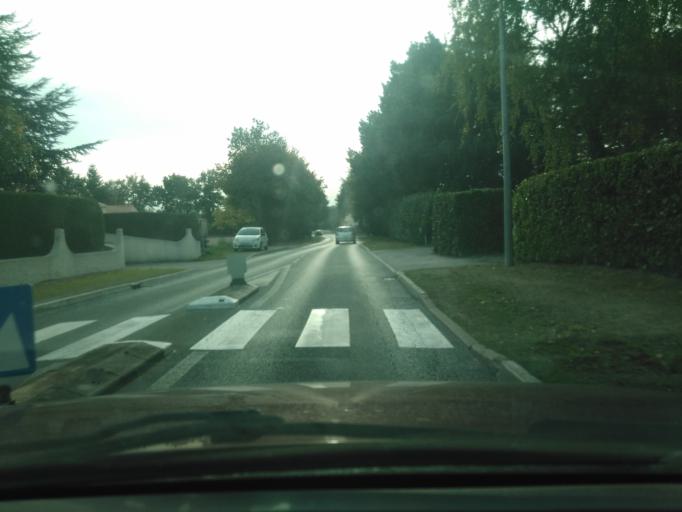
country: FR
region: Pays de la Loire
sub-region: Departement de la Vendee
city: Dompierre-sur-Yon
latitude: 46.7239
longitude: -1.4004
